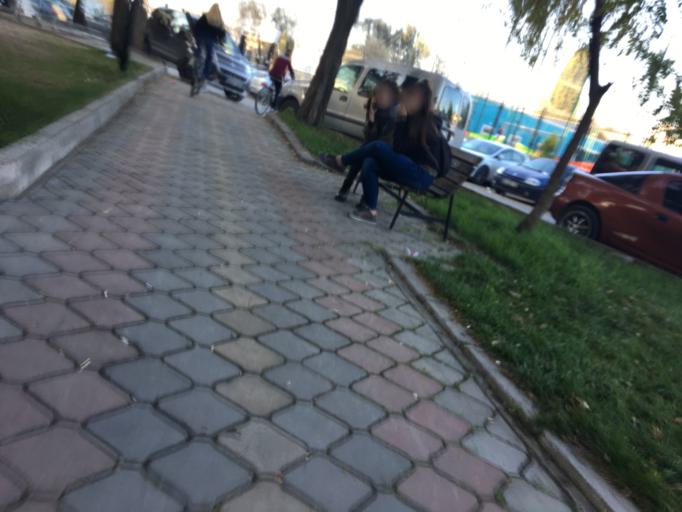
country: TR
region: Izmir
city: Buca
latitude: 38.3857
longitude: 27.1660
